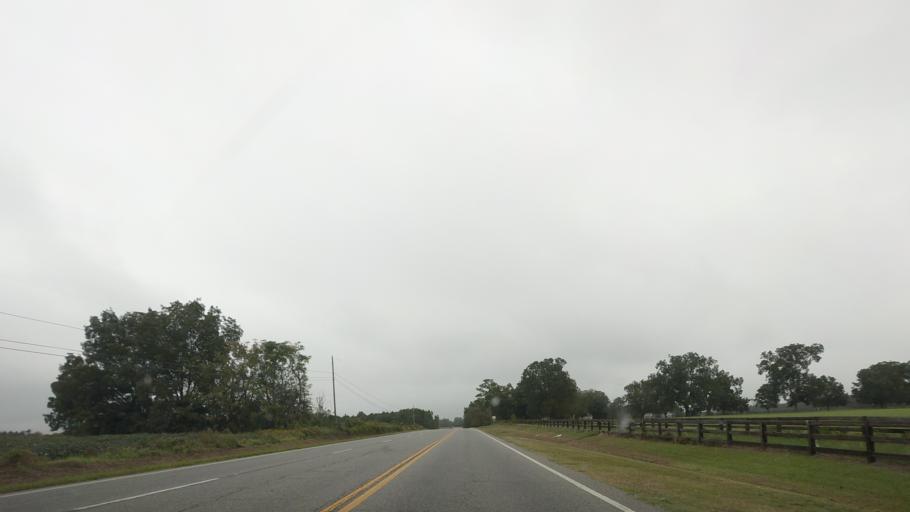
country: US
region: Georgia
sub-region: Ben Hill County
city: Fitzgerald
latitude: 31.6735
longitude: -83.2359
